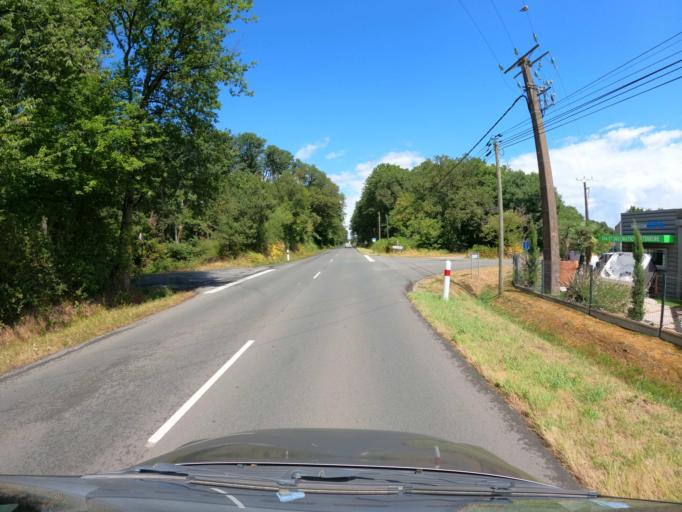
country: FR
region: Pays de la Loire
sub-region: Departement de Maine-et-Loire
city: Feneu
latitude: 47.5792
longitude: -0.5921
